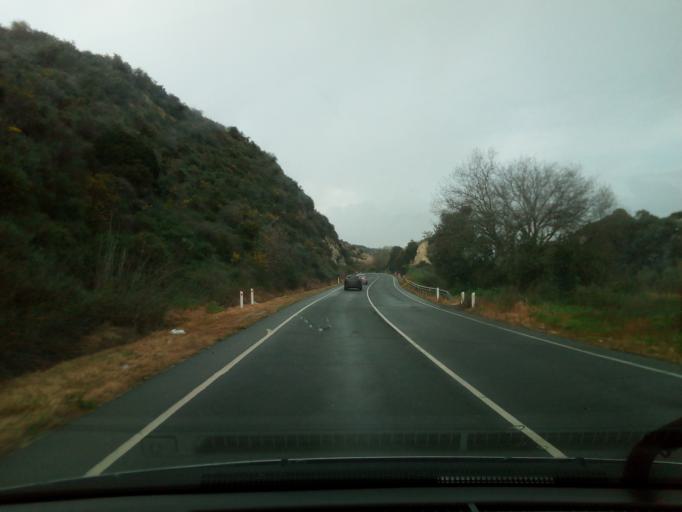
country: CY
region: Pafos
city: Polis
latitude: 34.9715
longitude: 32.4521
